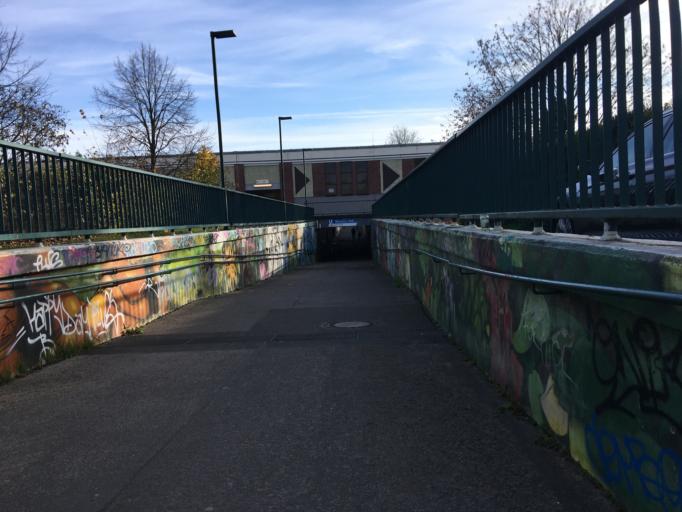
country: DE
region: Berlin
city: Biesdorf
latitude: 52.5005
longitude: 13.5472
